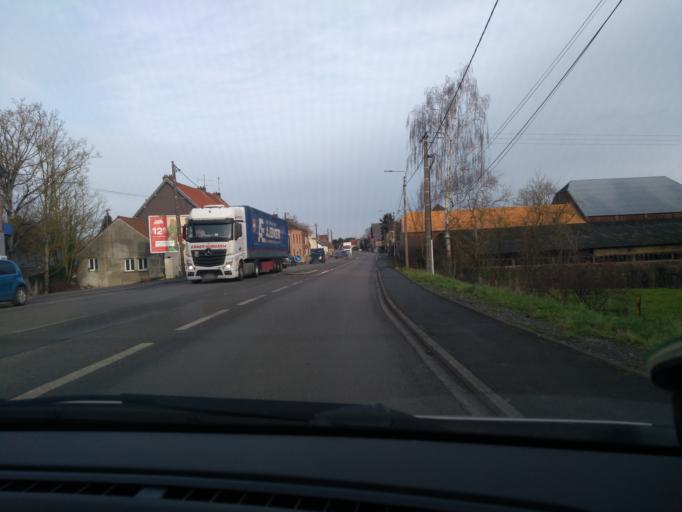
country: FR
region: Nord-Pas-de-Calais
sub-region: Departement du Nord
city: Maubeuge
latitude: 50.3089
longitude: 3.9770
